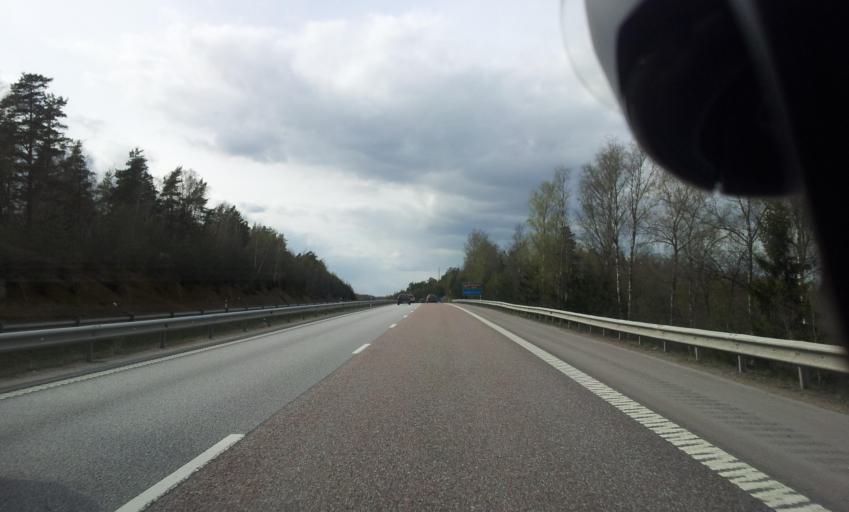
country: SE
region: Uppsala
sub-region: Habo Kommun
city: Balsta
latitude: 59.5789
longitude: 17.5350
